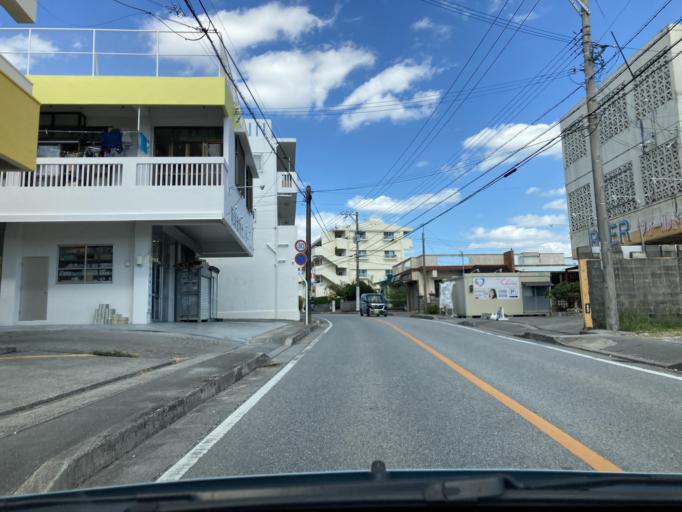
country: JP
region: Okinawa
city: Tomigusuku
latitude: 26.1860
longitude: 127.7271
